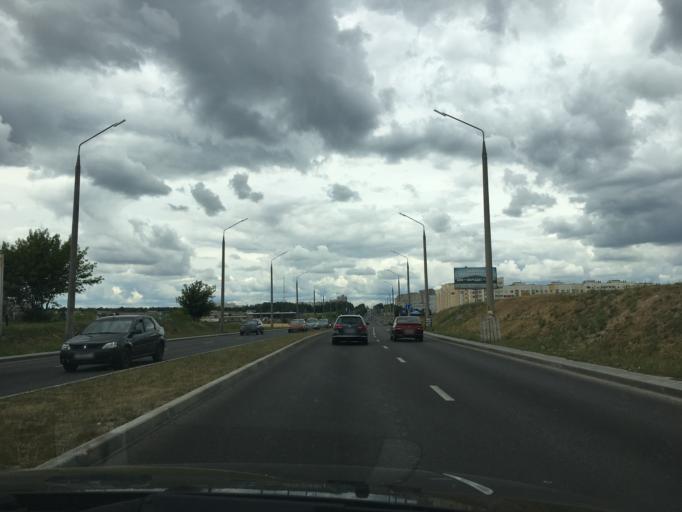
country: BY
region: Grodnenskaya
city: Hrodna
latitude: 53.6357
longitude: 23.8500
